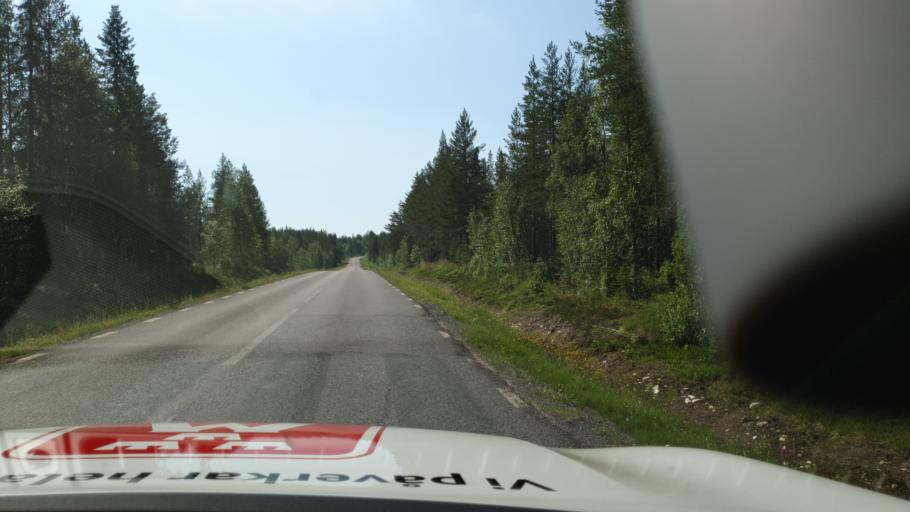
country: SE
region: Vaesterbotten
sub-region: Skelleftea Kommun
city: Langsele
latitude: 64.9987
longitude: 20.0904
